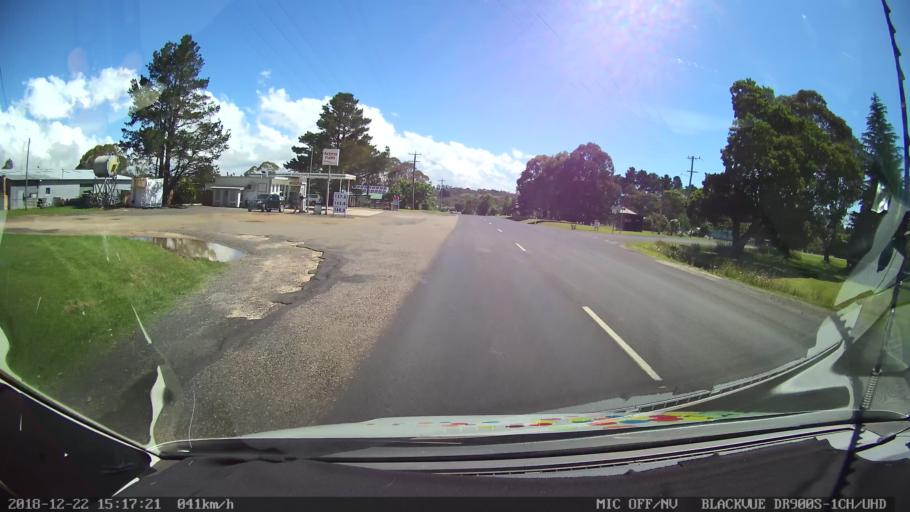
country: AU
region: New South Wales
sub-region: Bellingen
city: Dorrigo
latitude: -30.3974
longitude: 152.3529
